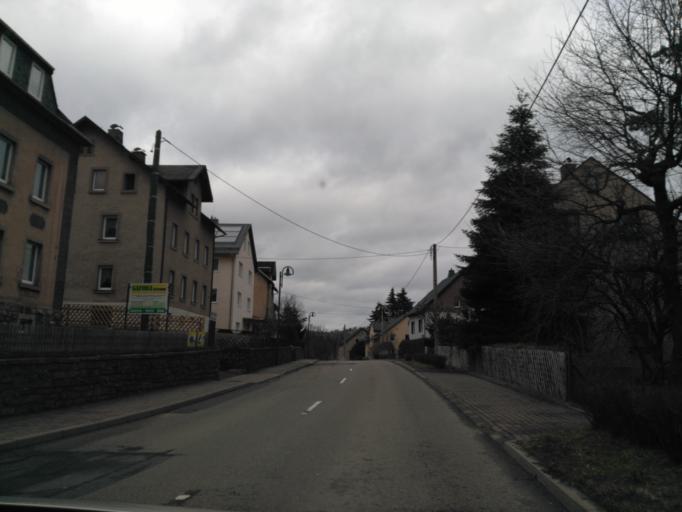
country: DE
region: Saxony
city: Venusberg
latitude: 50.7087
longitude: 12.9960
